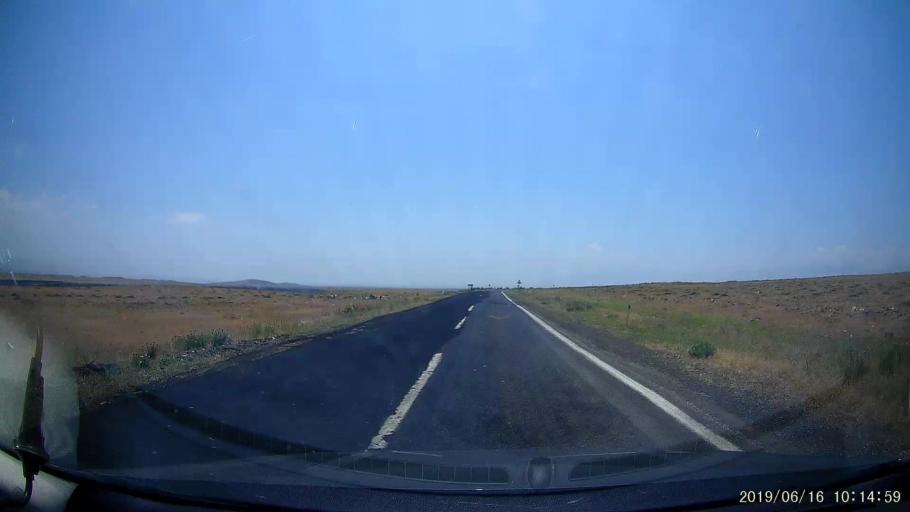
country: TR
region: Igdir
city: Tuzluca
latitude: 40.1801
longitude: 43.6738
